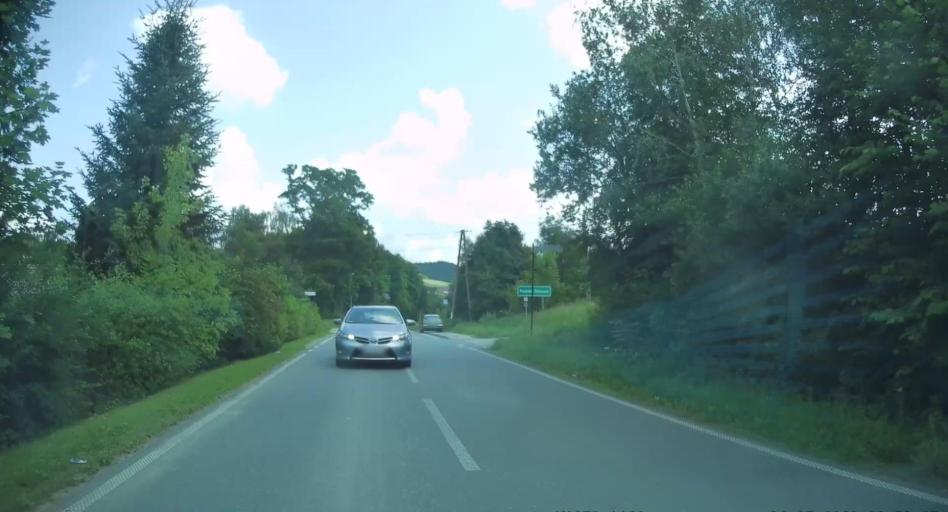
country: PL
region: Lesser Poland Voivodeship
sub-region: Powiat nowosadecki
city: Korzenna
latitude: 49.7526
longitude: 20.7736
